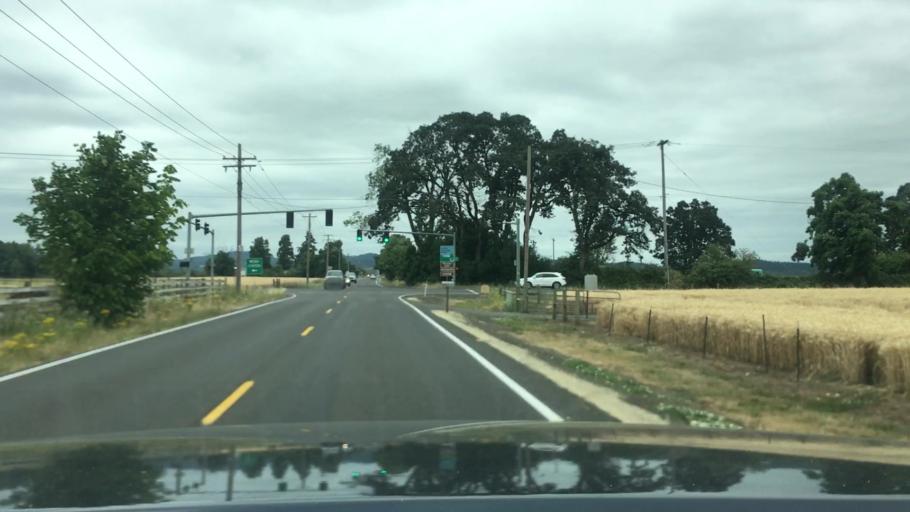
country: US
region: Oregon
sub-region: Lane County
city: Junction City
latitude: 44.1036
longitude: -123.2084
